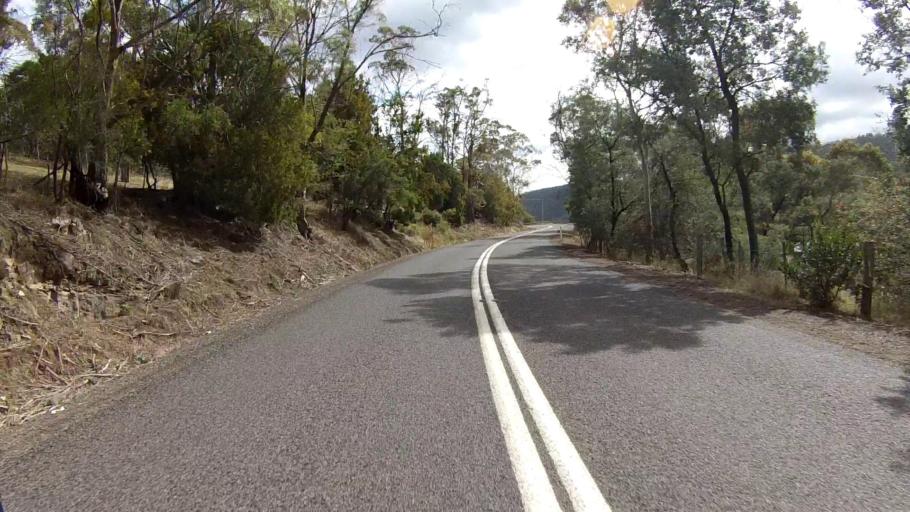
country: AU
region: Tasmania
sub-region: Clarence
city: Lindisfarne
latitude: -42.8051
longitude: 147.3544
